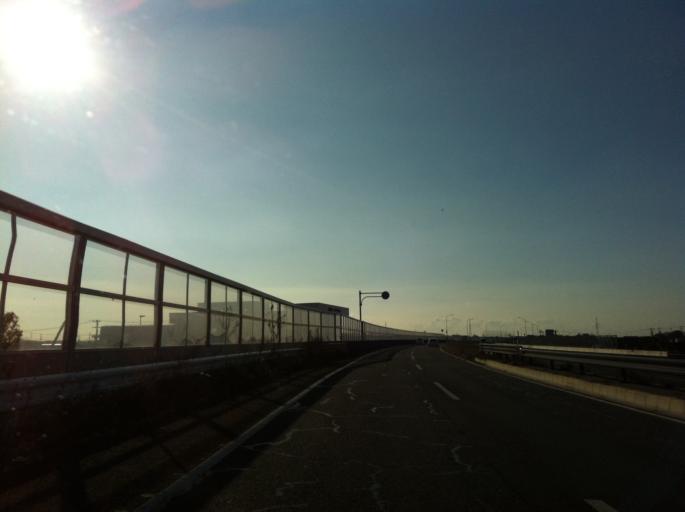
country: JP
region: Aichi
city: Toyohashi
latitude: 34.7283
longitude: 137.3545
